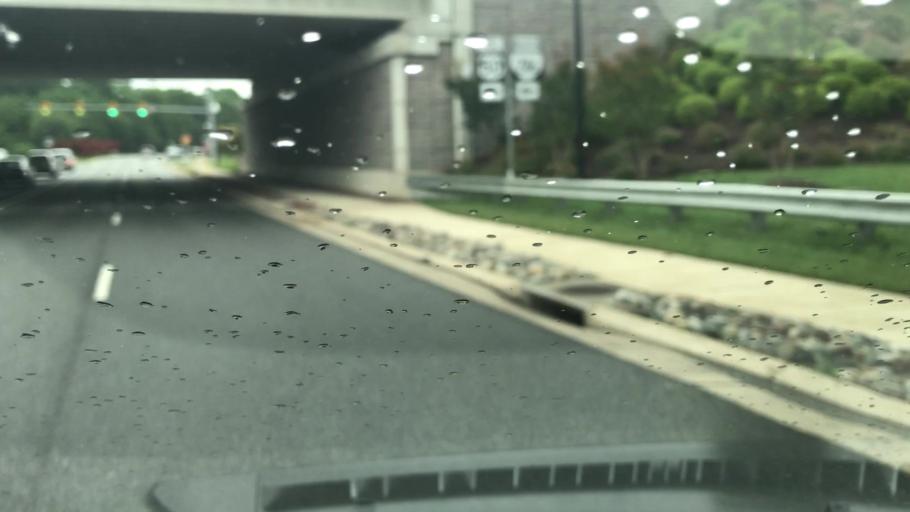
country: US
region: Virginia
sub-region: Fairfax County
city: Greenbriar
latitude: 38.8629
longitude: -77.3828
